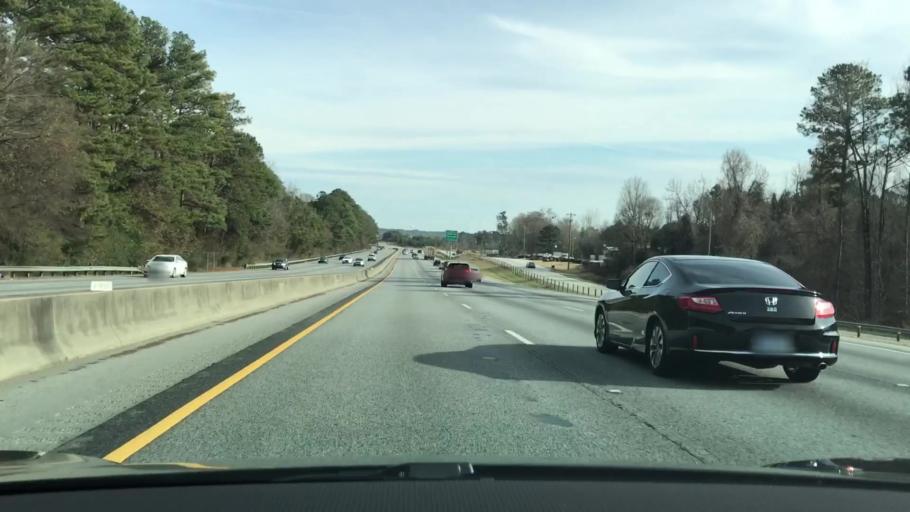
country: US
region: Georgia
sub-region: Newton County
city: Porterdale
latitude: 33.6212
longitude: -83.9330
